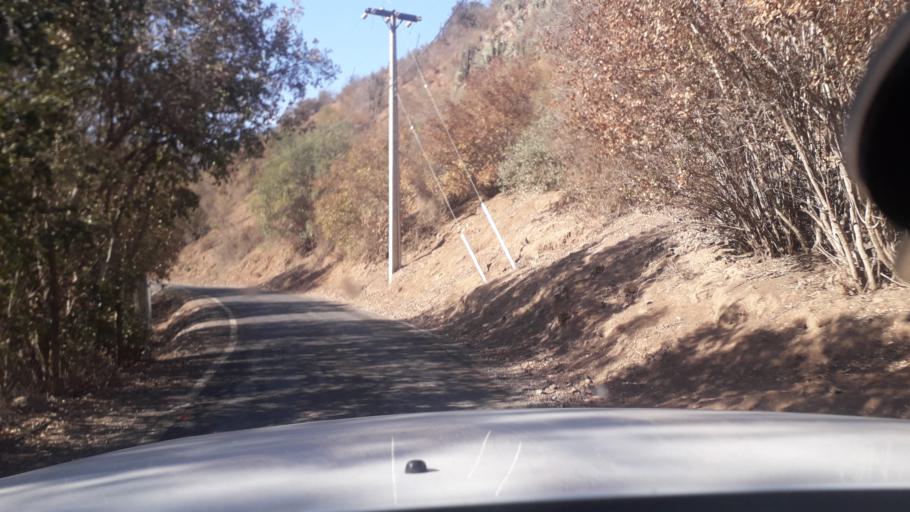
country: CL
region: Valparaiso
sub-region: Provincia de Marga Marga
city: Limache
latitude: -33.0704
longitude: -71.0981
